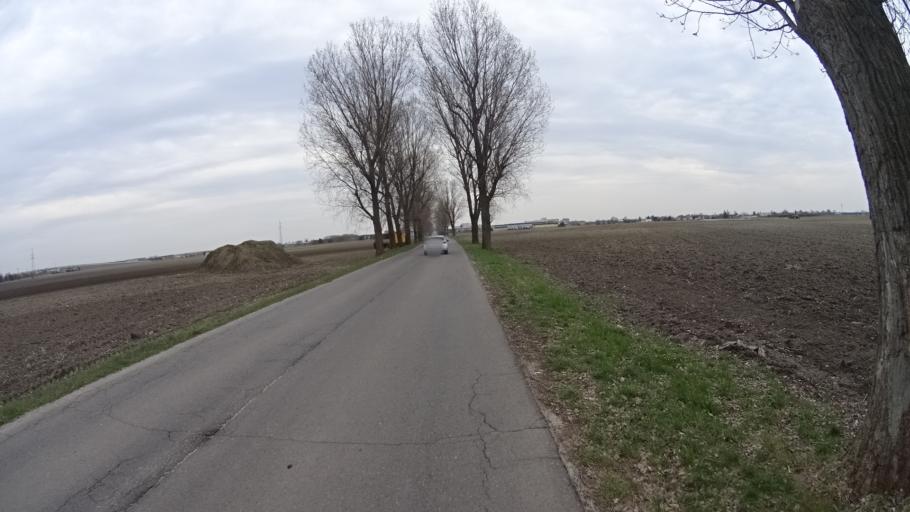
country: PL
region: Masovian Voivodeship
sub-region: Powiat warszawski zachodni
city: Ozarow Mazowiecki
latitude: 52.2059
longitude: 20.8198
